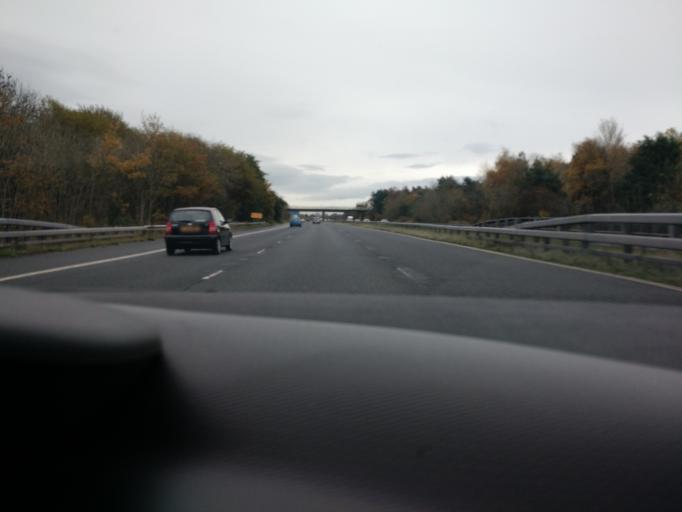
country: GB
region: England
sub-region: Lancashire
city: Preston
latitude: 53.7983
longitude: -2.7382
